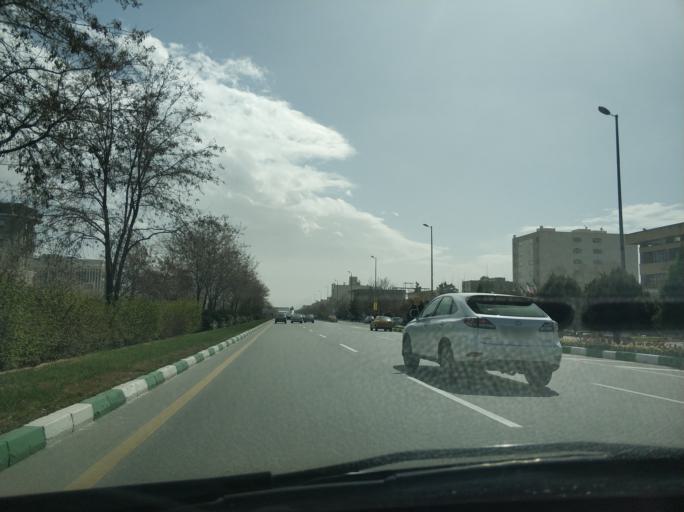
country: IR
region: Razavi Khorasan
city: Mashhad
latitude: 36.3365
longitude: 59.4715
